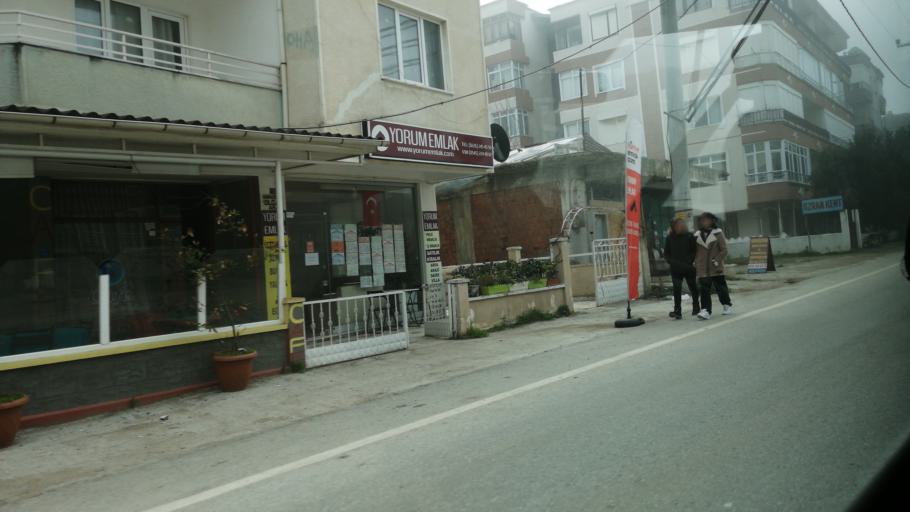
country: TR
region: Yalova
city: Cinarcik
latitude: 40.6433
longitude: 29.0866
